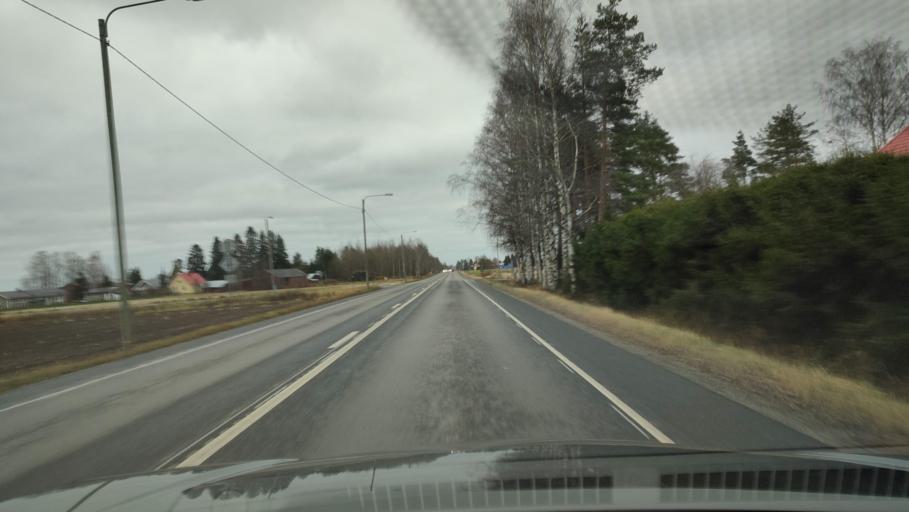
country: FI
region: Southern Ostrobothnia
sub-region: Seinaejoki
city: Ilmajoki
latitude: 62.6938
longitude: 22.5001
